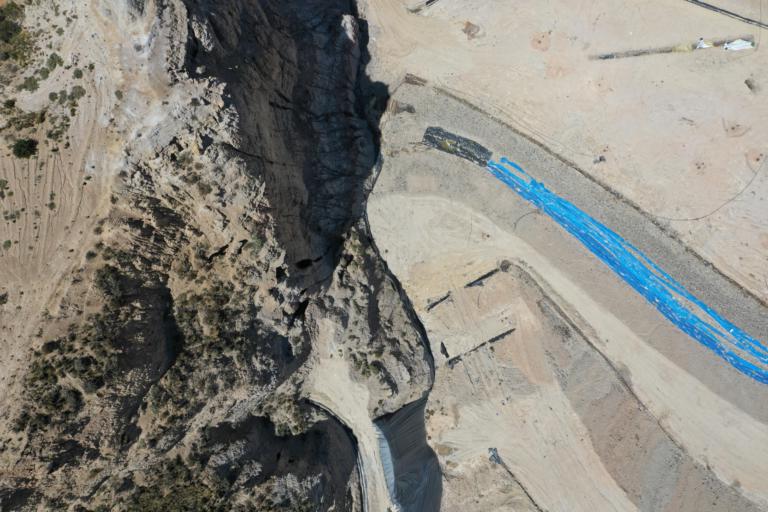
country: BO
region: La Paz
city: La Paz
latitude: -16.5553
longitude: -68.1246
